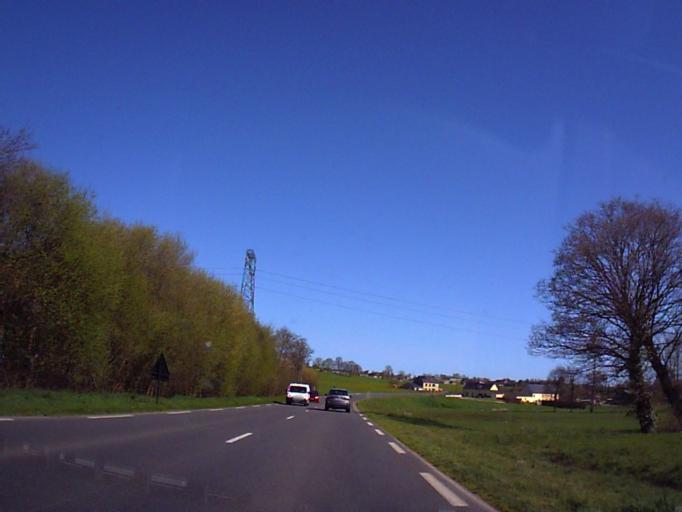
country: FR
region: Brittany
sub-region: Departement d'Ille-et-Vilaine
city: Quedillac
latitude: 48.2548
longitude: -2.1675
